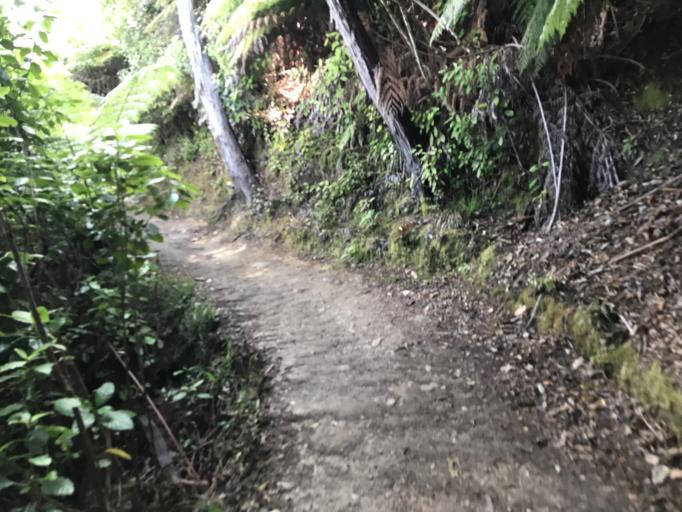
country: NZ
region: Marlborough
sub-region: Marlborough District
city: Picton
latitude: -41.2626
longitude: 173.9285
